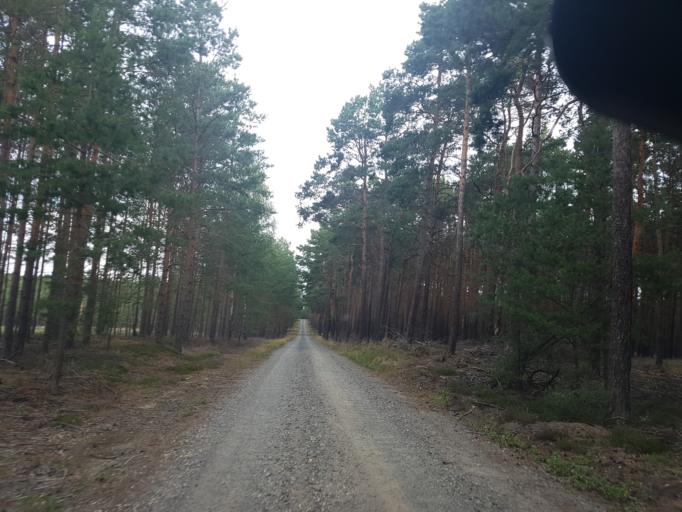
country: DE
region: Brandenburg
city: Sallgast
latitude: 51.6232
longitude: 13.8058
